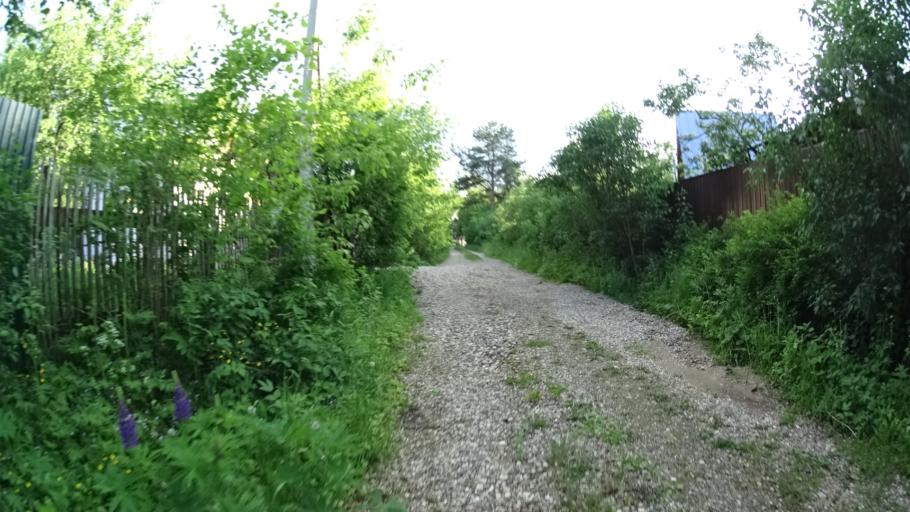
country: RU
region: Moskovskaya
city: Zelenogradskiy
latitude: 56.0969
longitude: 37.9228
